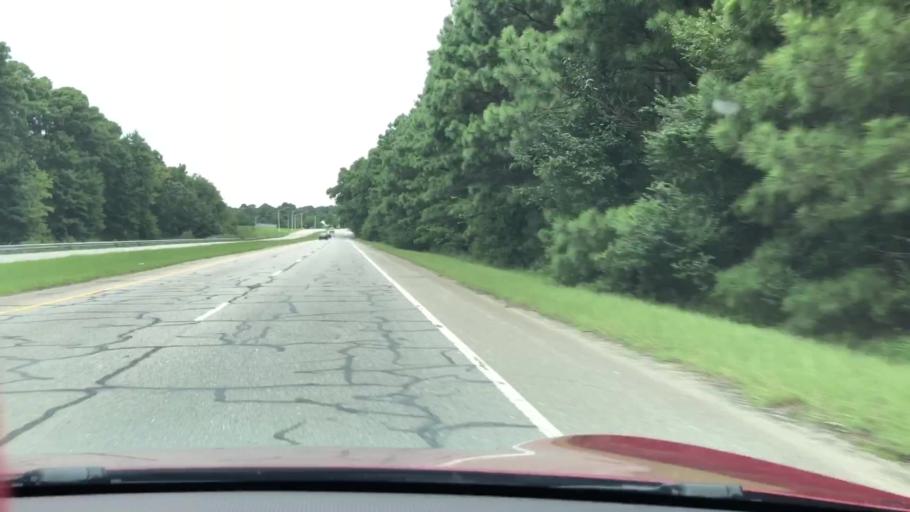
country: US
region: Virginia
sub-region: City of Virginia Beach
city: Virginia Beach
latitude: 36.8324
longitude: -76.0116
